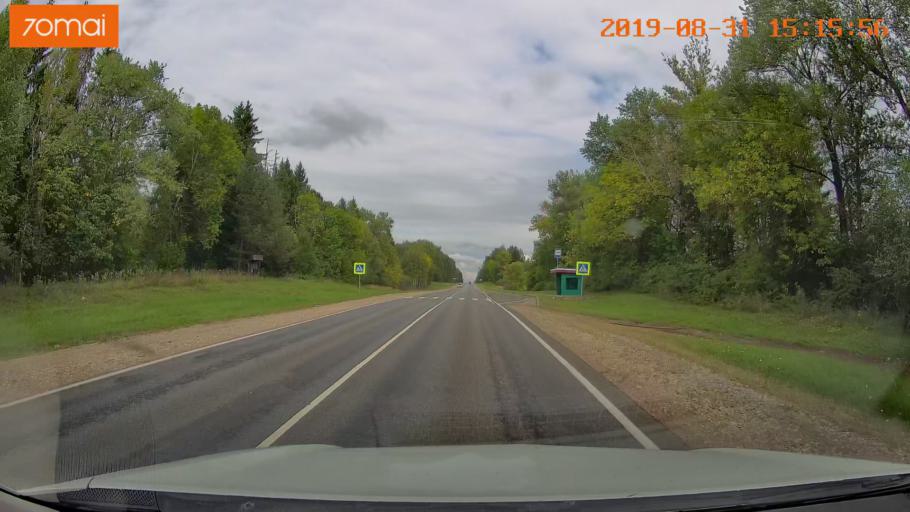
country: RU
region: Kaluga
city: Baryatino
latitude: 54.4556
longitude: 34.3382
